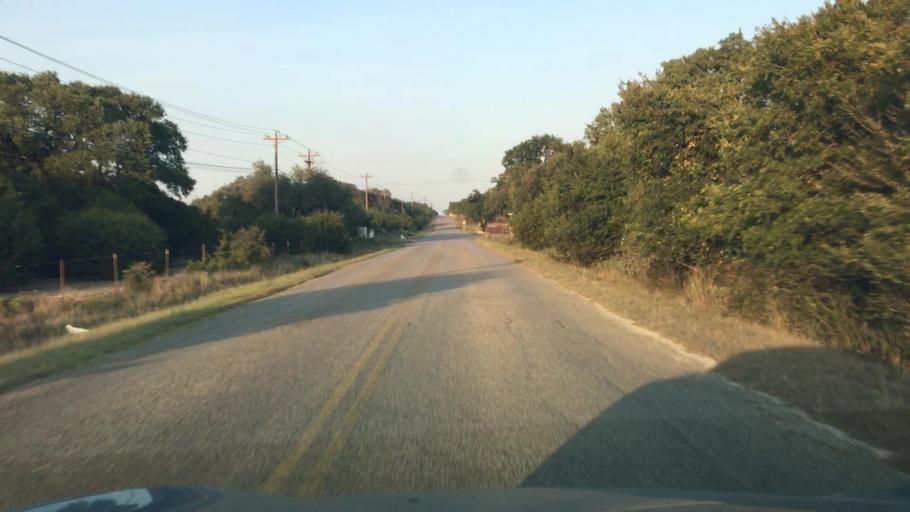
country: US
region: Texas
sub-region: Hays County
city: Dripping Springs
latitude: 30.1532
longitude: -98.0201
